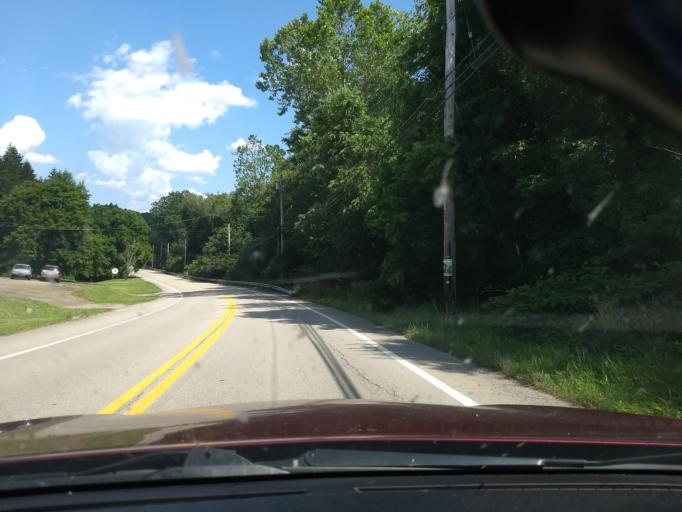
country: US
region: Pennsylvania
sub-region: Westmoreland County
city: Trafford
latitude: 40.3725
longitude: -79.7596
